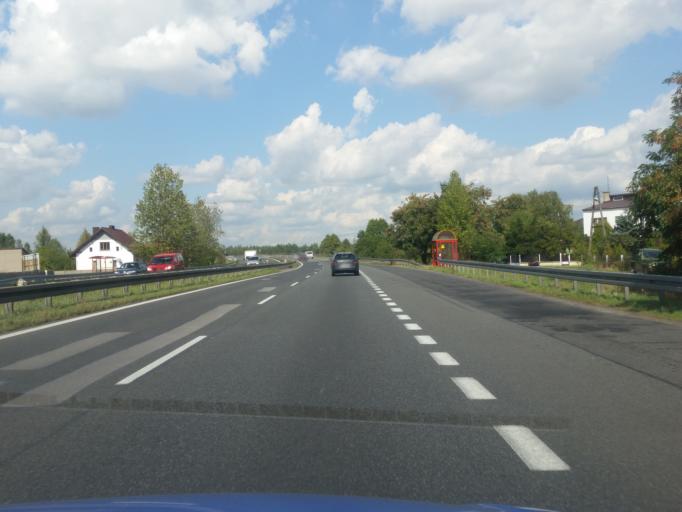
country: PL
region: Silesian Voivodeship
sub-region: Powiat bedzinski
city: Siewierz
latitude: 50.4740
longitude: 19.2285
